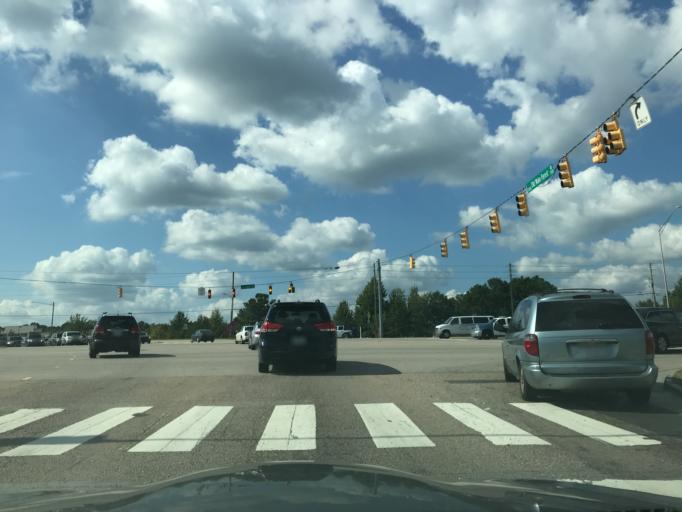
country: US
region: North Carolina
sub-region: Wake County
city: Raleigh
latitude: 35.8707
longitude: -78.5801
